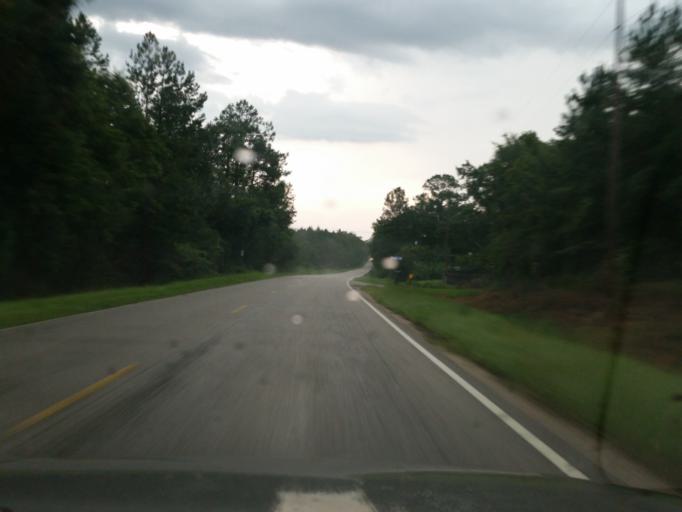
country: US
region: Florida
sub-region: Escambia County
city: Cantonment
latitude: 30.6093
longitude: -87.4114
